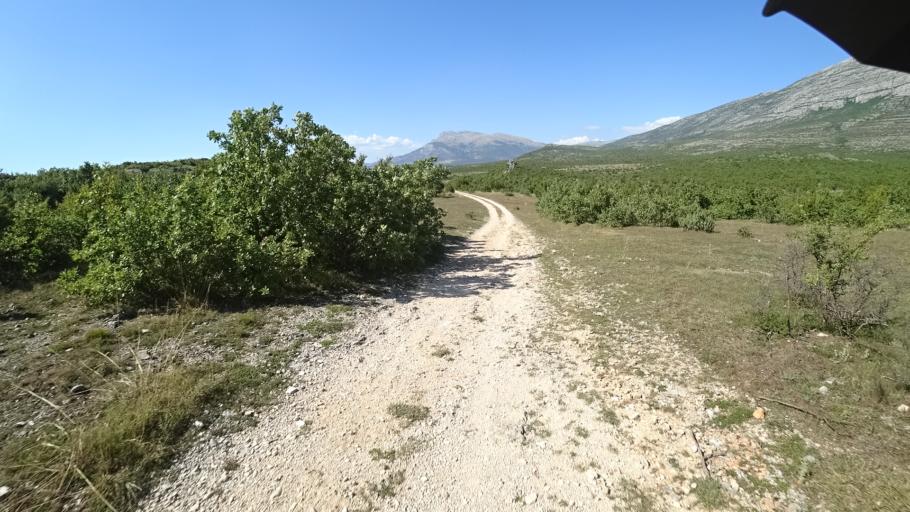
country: HR
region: Splitsko-Dalmatinska
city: Hrvace
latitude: 43.9404
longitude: 16.4565
